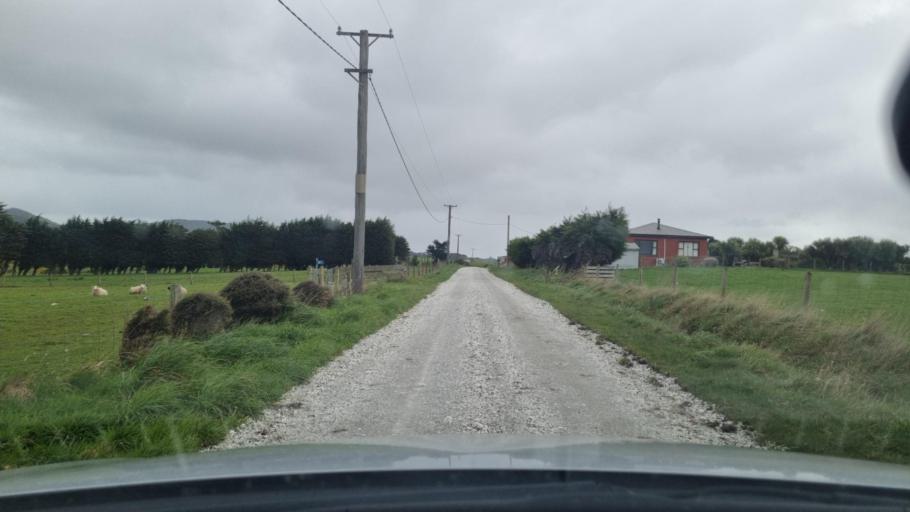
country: NZ
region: Southland
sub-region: Invercargill City
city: Bluff
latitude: -46.5421
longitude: 168.2933
